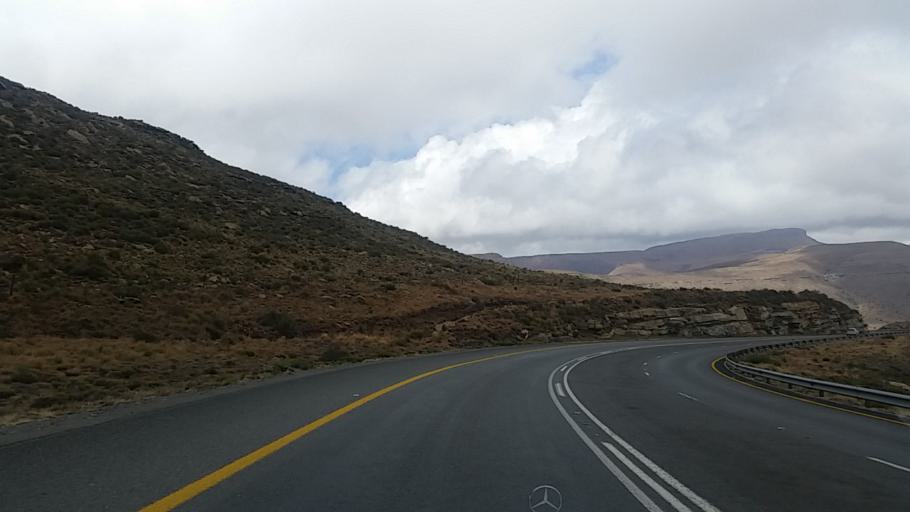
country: ZA
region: Eastern Cape
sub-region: Chris Hani District Municipality
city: Middelburg
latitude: -31.8389
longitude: 24.8652
